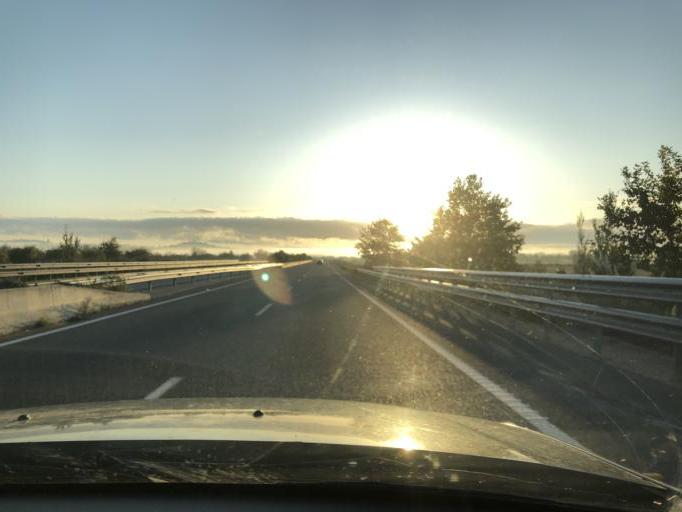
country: ES
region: Balearic Islands
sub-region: Illes Balears
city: Montuiri
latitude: 39.5630
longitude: 2.9571
